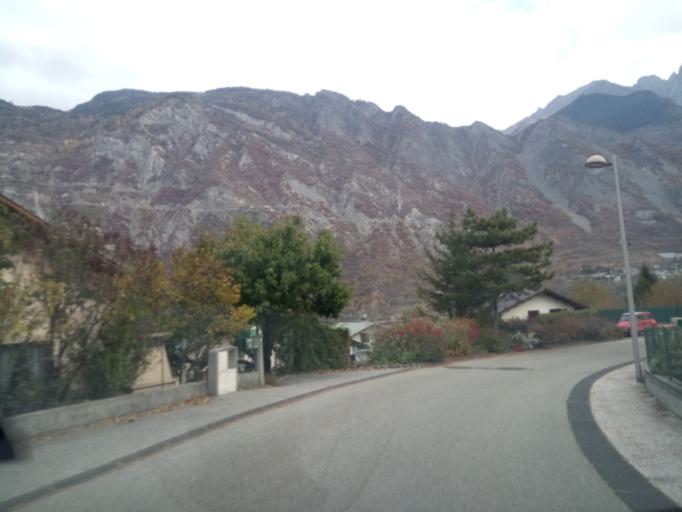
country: FR
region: Rhone-Alpes
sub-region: Departement de la Savoie
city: Villargondran
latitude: 45.2627
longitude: 6.3770
